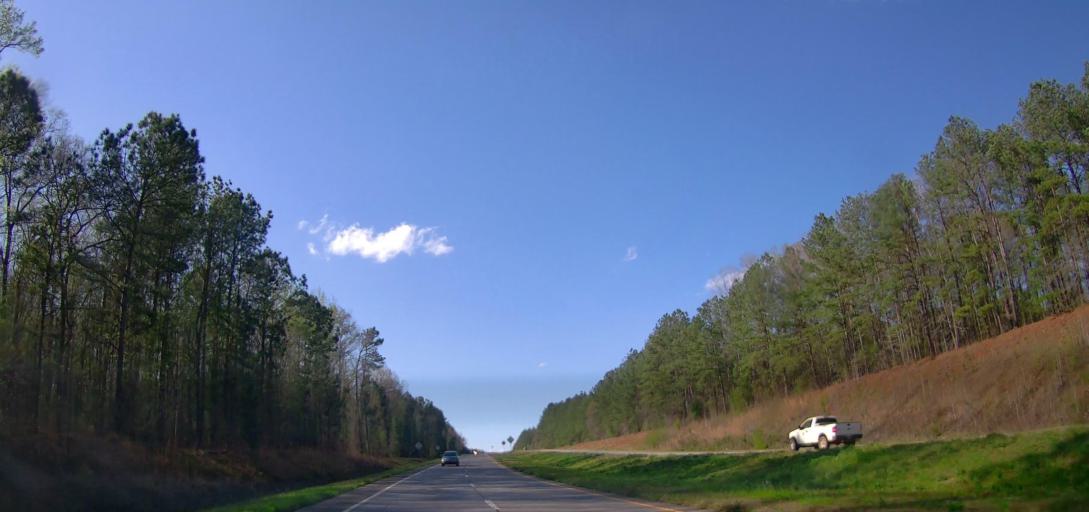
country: US
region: Georgia
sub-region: Baldwin County
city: Hardwick
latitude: 33.0355
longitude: -83.2516
